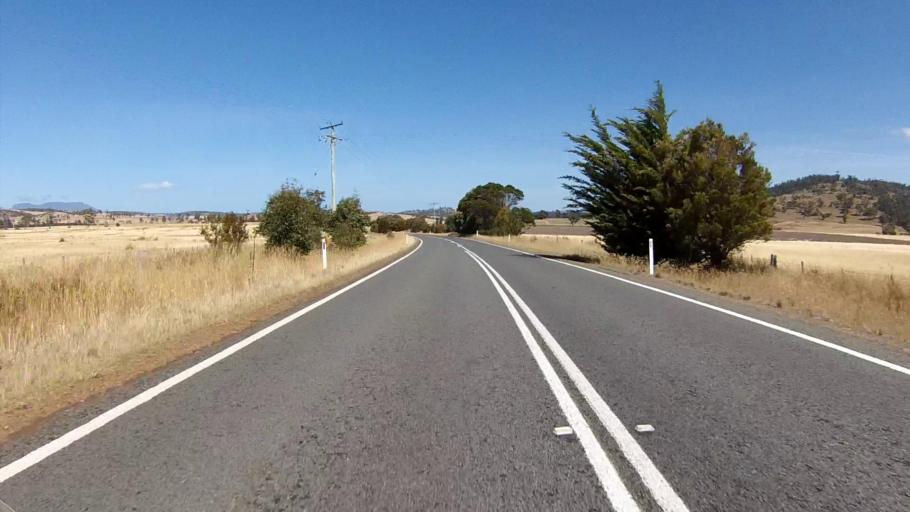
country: AU
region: Tasmania
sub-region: Sorell
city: Sorell
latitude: -42.4418
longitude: 147.9271
